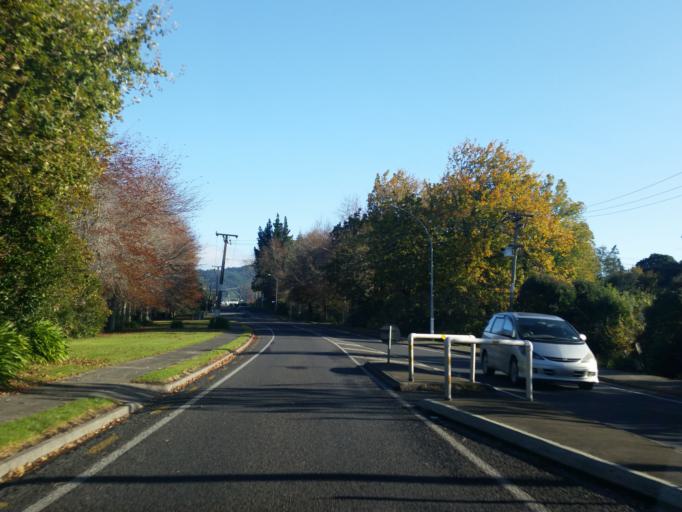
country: NZ
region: Bay of Plenty
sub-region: Western Bay of Plenty District
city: Katikati
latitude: -37.5505
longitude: 175.9164
